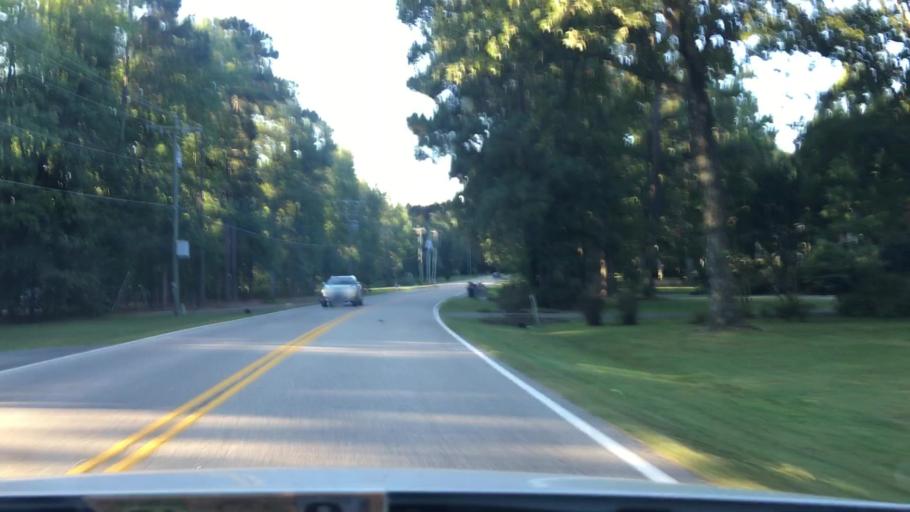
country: US
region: Virginia
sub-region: Chesterfield County
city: Bon Air
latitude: 37.5296
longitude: -77.6412
